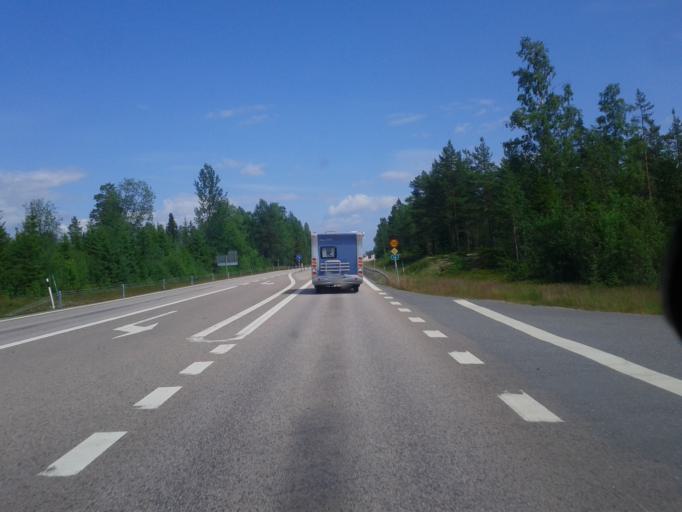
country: SE
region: Vaesternorrland
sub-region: OErnskoeldsviks Kommun
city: Husum
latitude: 63.4804
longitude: 19.2963
